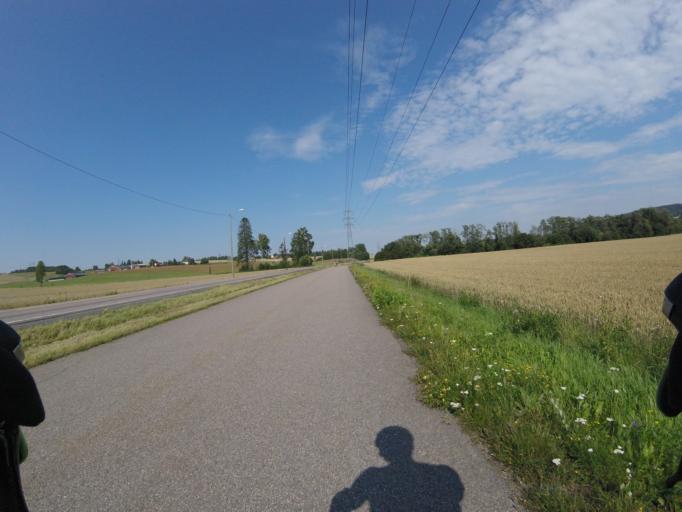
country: NO
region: Akershus
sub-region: Skedsmo
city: Leirsund
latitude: 59.9872
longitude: 11.0729
